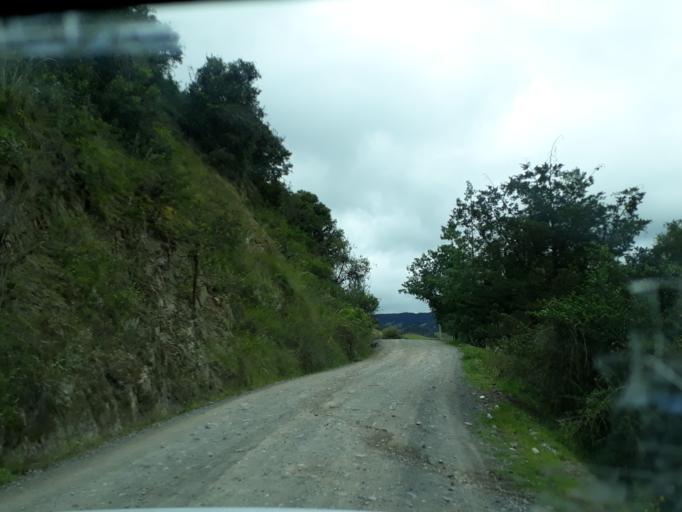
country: CO
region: Cundinamarca
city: Carmen de Carupa
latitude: 5.3134
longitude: -73.8960
